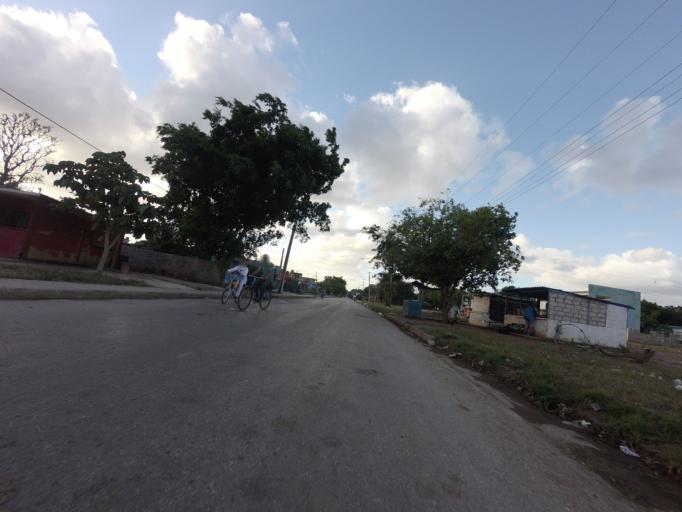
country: CU
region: Ciego de Avila
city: Ciego de Avila
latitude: 21.8295
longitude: -78.7528
